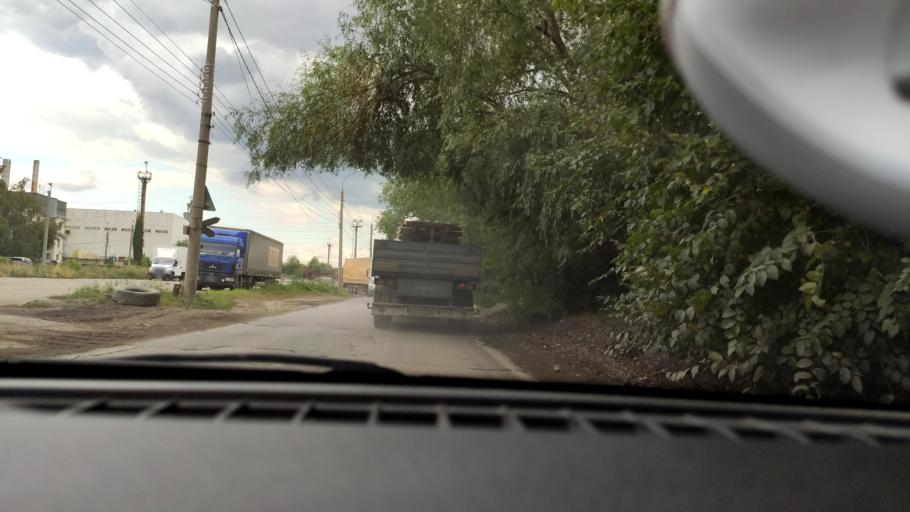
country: RU
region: Samara
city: Novokuybyshevsk
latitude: 53.1102
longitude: 50.0444
